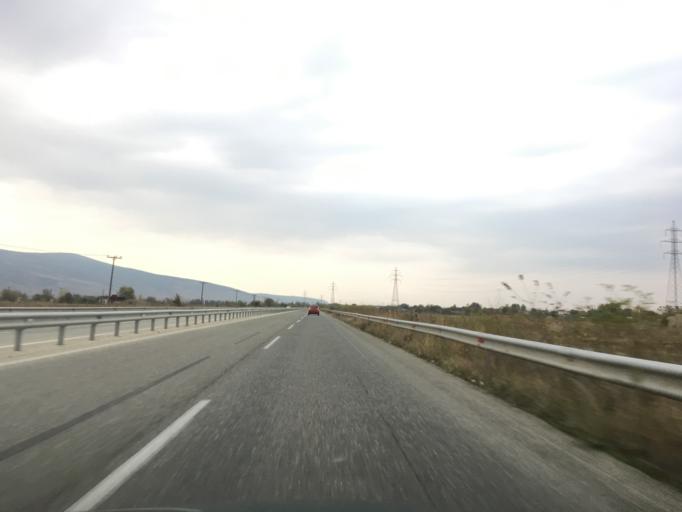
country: GR
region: Thessaly
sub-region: Trikala
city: Megalochori
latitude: 39.5669
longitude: 21.8344
